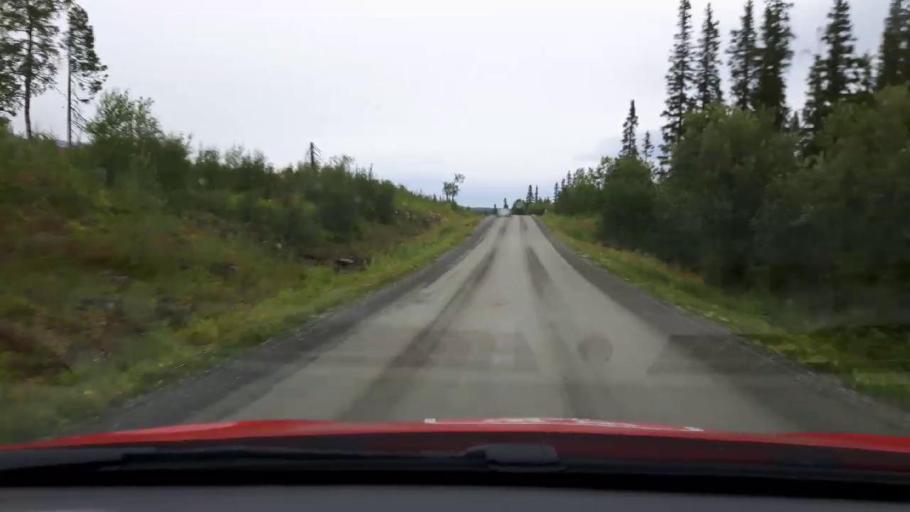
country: SE
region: Jaemtland
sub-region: Are Kommun
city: Are
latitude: 63.4168
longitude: 13.2276
